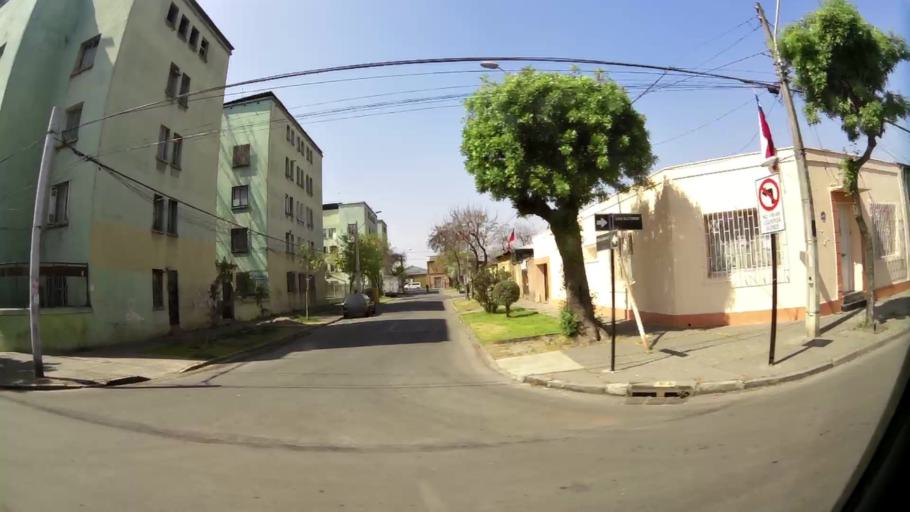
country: CL
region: Santiago Metropolitan
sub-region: Provincia de Santiago
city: Santiago
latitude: -33.4729
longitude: -70.6729
